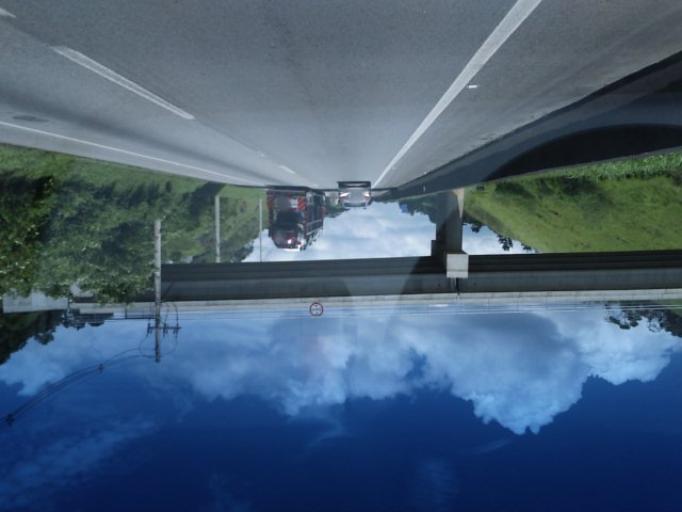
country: BR
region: Sao Paulo
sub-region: Juquitiba
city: Juquitiba
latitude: -23.9562
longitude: -47.1109
